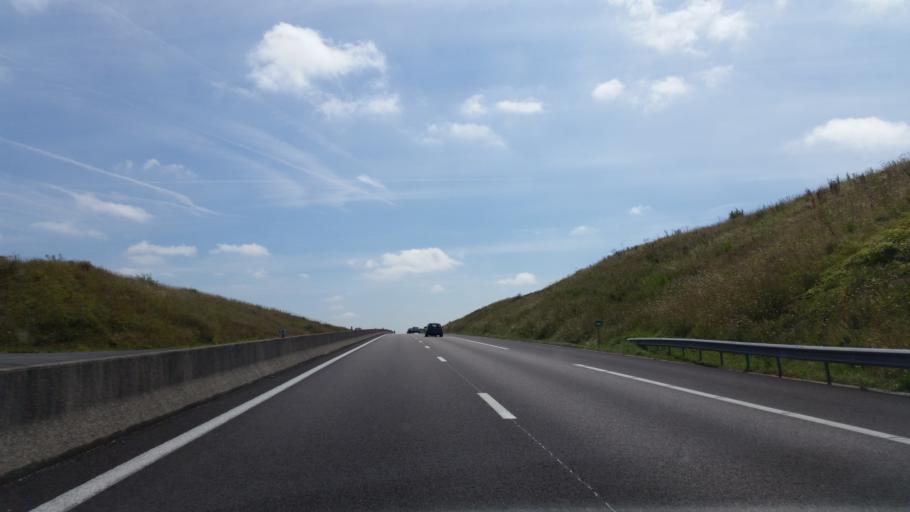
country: FR
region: Haute-Normandie
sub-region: Departement de la Seine-Maritime
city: Neufchatel-en-Bray
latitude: 49.7388
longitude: 1.5428
